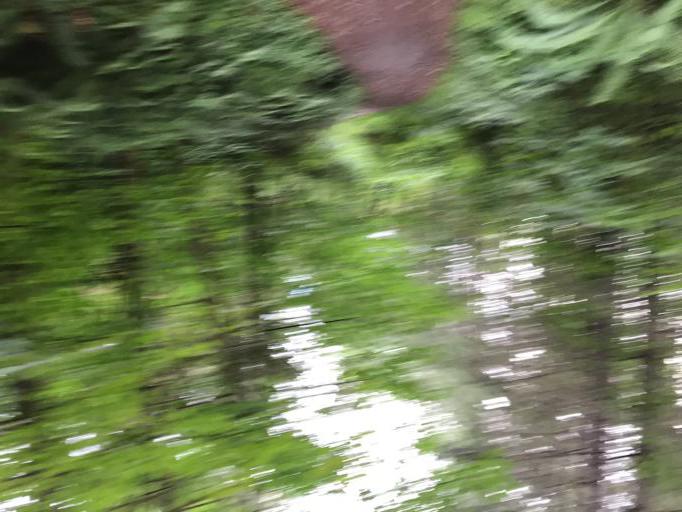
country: US
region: Washington
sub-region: King County
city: Ravensdale
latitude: 47.3468
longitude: -122.0072
